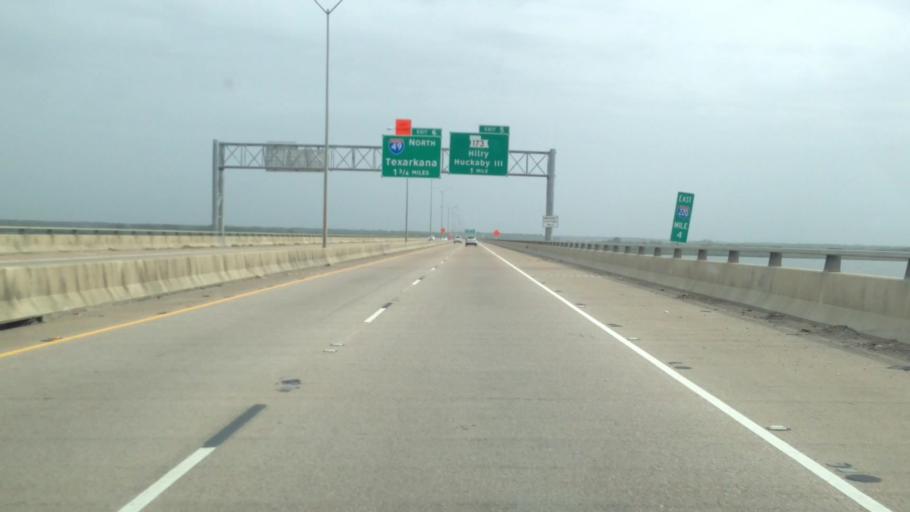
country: US
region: Louisiana
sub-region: Caddo Parish
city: Shreveport
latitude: 32.5073
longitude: -93.8152
